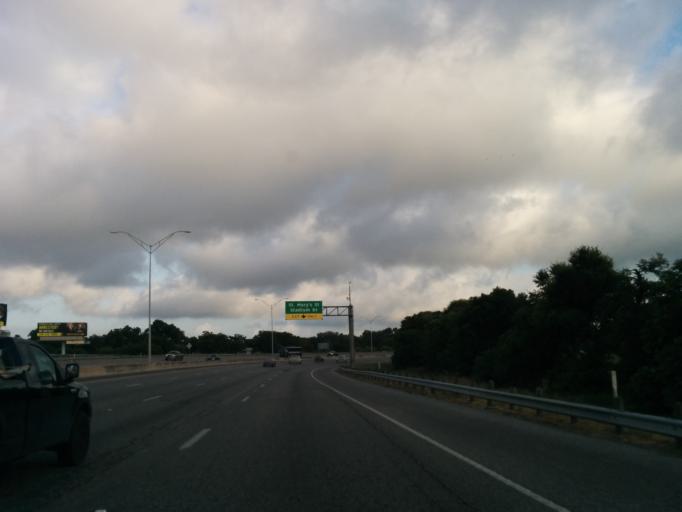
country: US
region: Texas
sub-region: Bexar County
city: San Antonio
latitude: 29.4478
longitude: -98.4811
